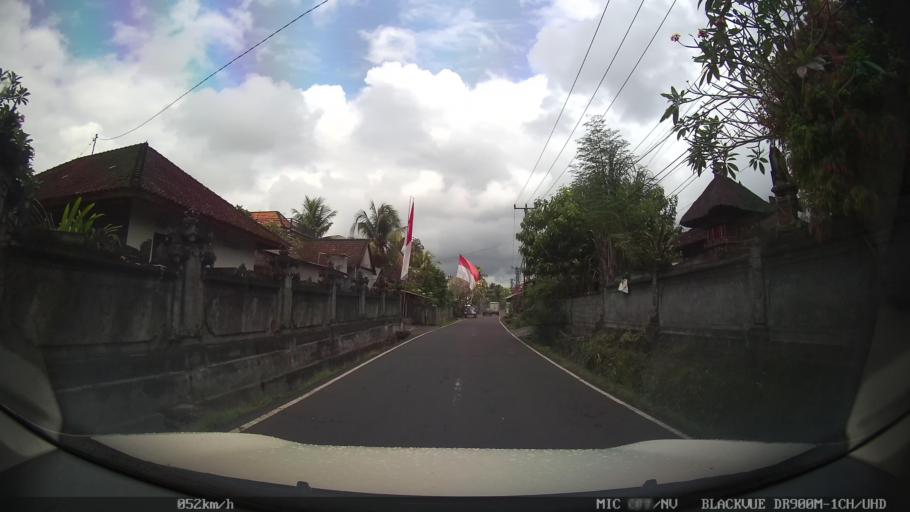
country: ID
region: Bali
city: Banjar Jumbayah
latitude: -8.5592
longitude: 115.1792
